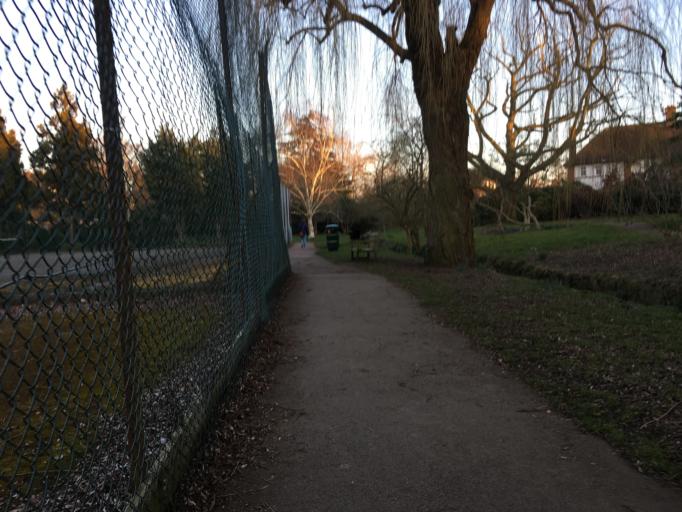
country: GB
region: England
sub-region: Greater London
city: Hendon
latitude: 51.5853
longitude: -0.1851
